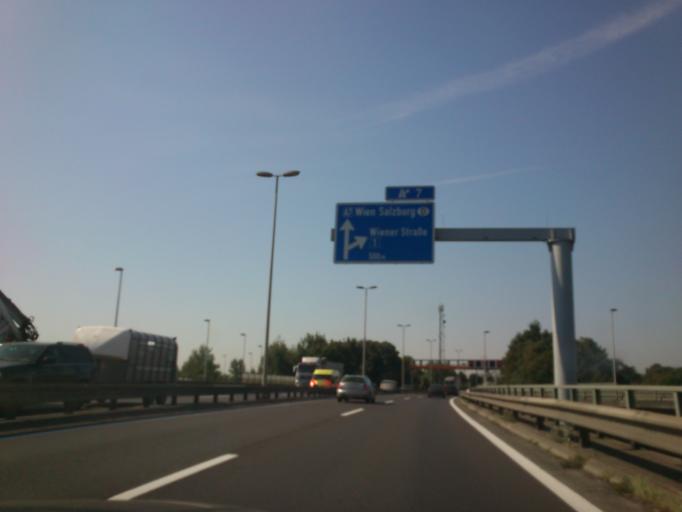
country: AT
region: Upper Austria
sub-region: Linz Stadt
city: Linz
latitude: 48.2877
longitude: 14.3180
